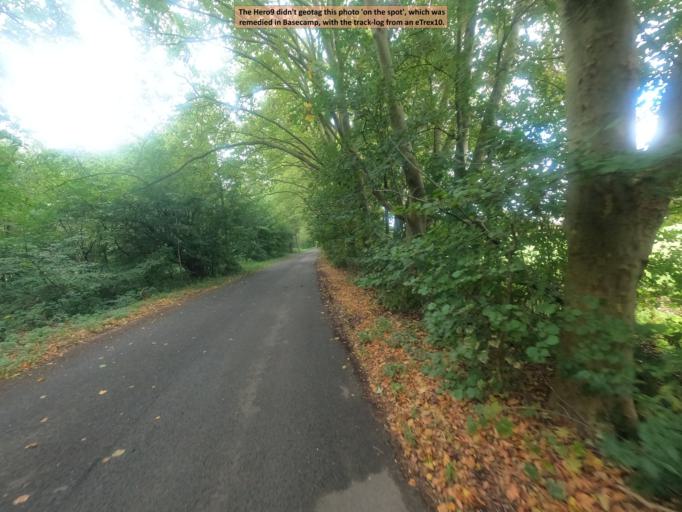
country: BE
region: Flanders
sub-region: Provincie Antwerpen
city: Oostmalle
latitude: 51.2661
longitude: 4.7741
